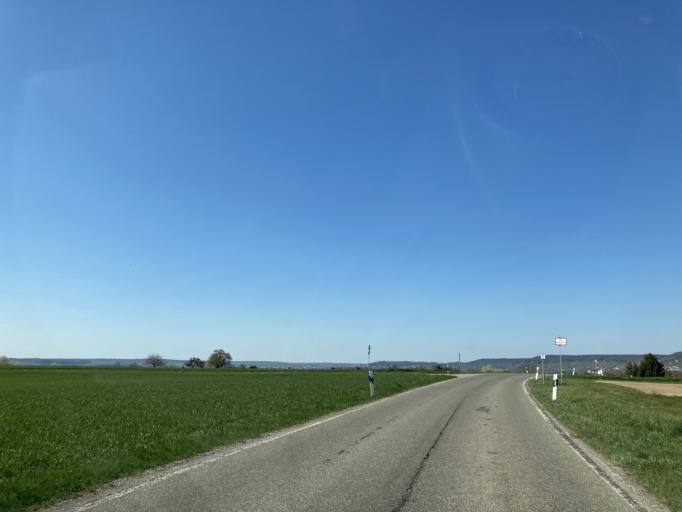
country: DE
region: Baden-Wuerttemberg
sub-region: Tuebingen Region
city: Rottenburg
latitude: 48.5354
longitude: 8.9187
